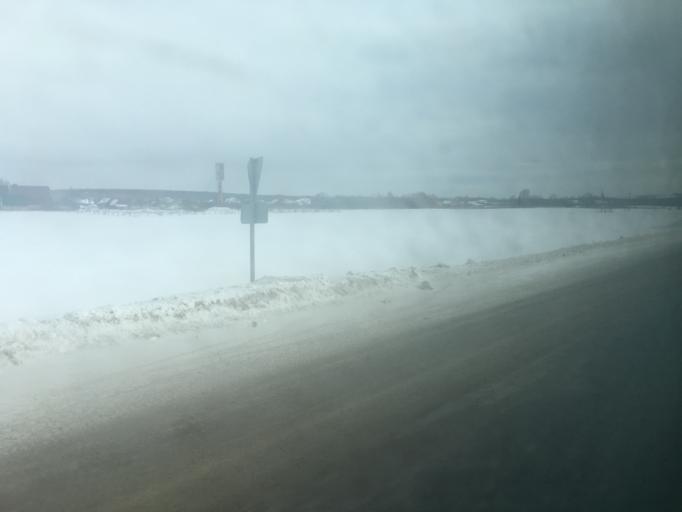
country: RU
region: Tatarstan
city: Nizhniye Vyazovyye
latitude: 55.7618
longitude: 48.5382
